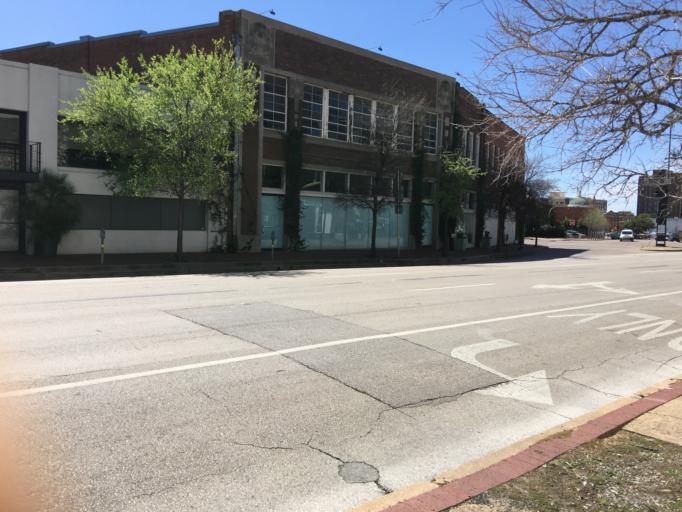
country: US
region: Texas
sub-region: Dallas County
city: Dallas
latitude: 32.7819
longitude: -96.7901
